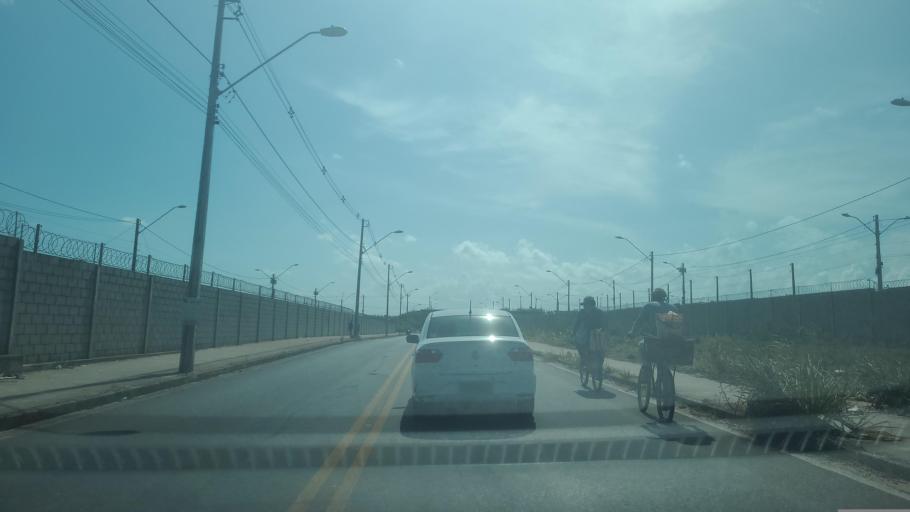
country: BR
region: Alagoas
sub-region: Satuba
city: Satuba
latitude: -9.5257
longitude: -35.7758
